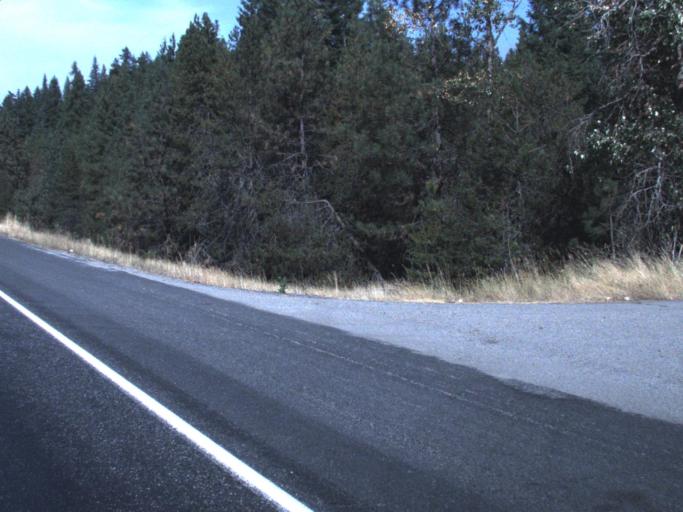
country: US
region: Washington
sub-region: Spokane County
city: Deer Park
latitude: 48.0721
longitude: -117.3326
